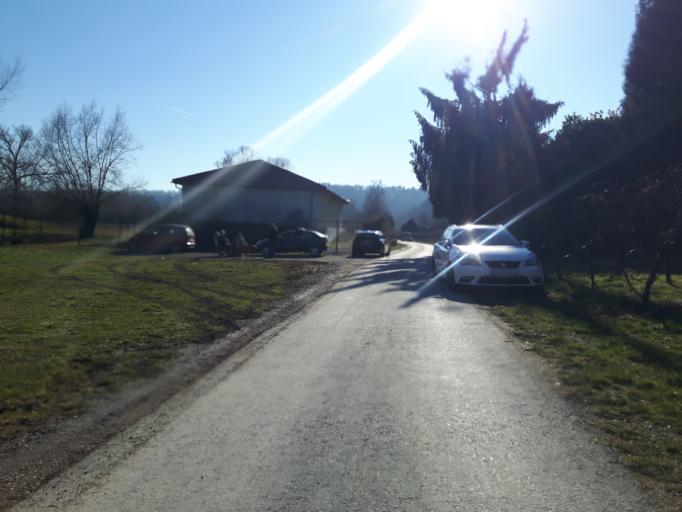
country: DE
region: Baden-Wuerttemberg
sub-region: Regierungsbezirk Stuttgart
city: Lauffen am Neckar
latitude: 49.0724
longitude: 9.1301
